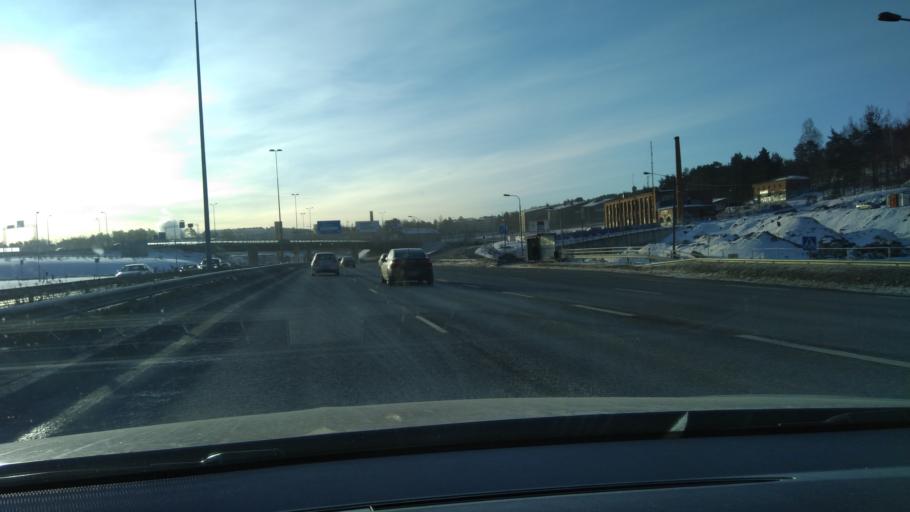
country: FI
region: Pirkanmaa
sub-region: Tampere
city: Tampere
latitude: 61.5042
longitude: 23.7213
